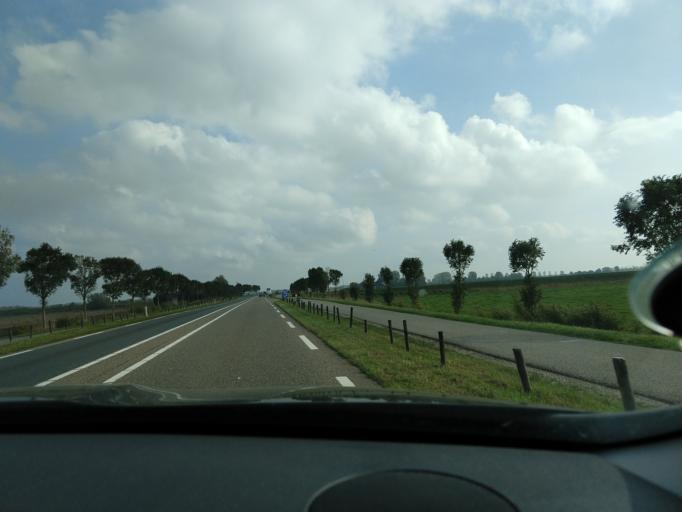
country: NL
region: Zeeland
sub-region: Schouwen-Duiveland
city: Scharendijke
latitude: 51.6502
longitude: 3.9507
